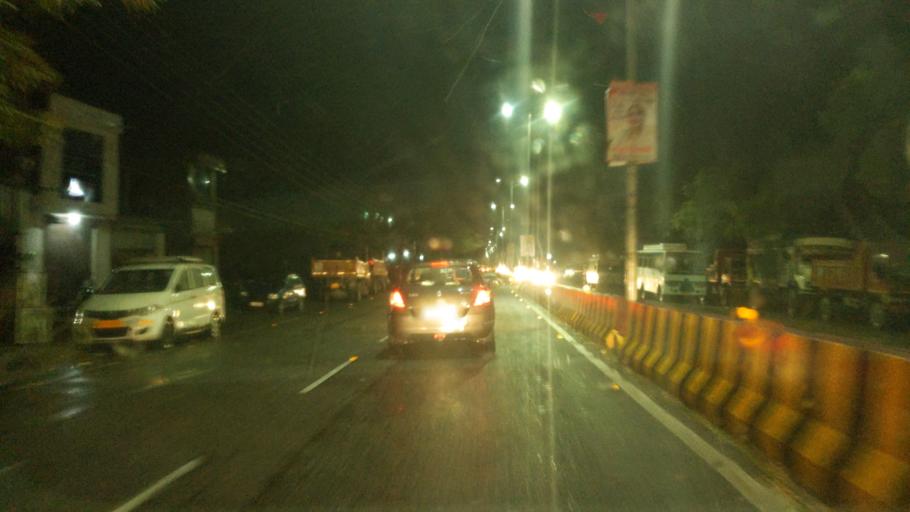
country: IN
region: Uttarakhand
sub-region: Naini Tal
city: Haldwani
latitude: 29.2556
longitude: 79.5424
